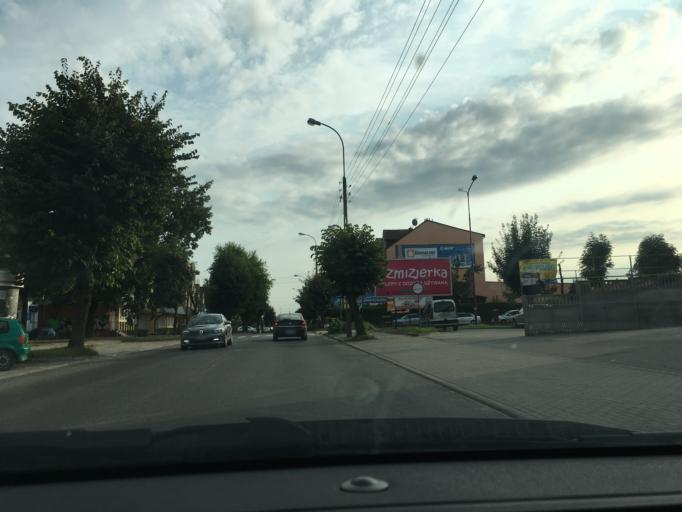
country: PL
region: Podlasie
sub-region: Powiat augustowski
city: Augustow
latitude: 53.8398
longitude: 22.9749
